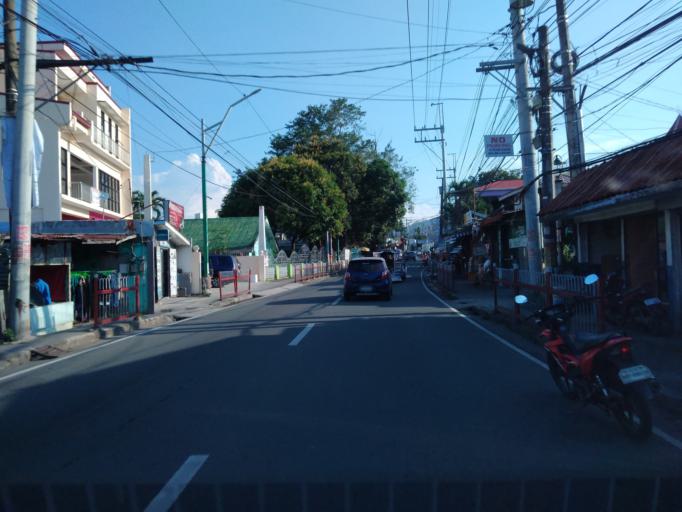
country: PH
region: Calabarzon
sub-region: Province of Laguna
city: Los Banos
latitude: 14.1747
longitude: 121.2432
